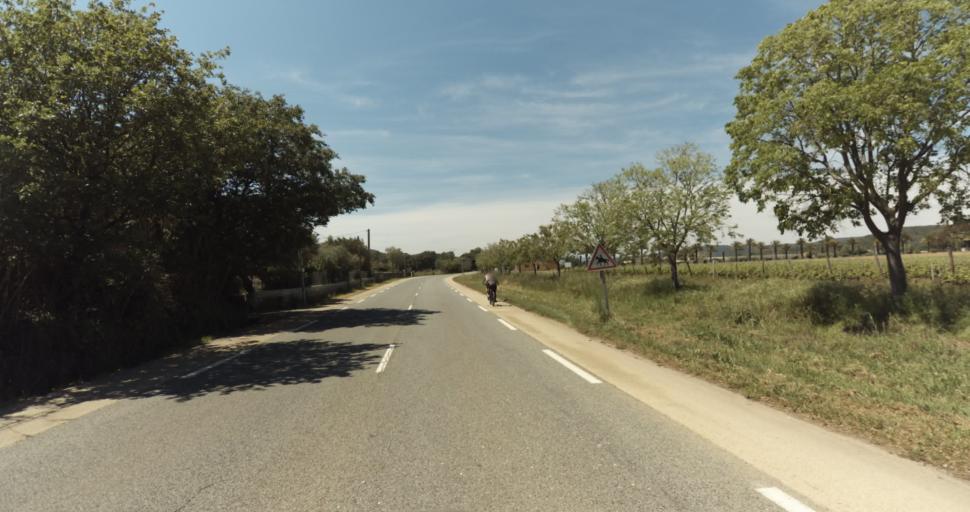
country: FR
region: Provence-Alpes-Cote d'Azur
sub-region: Departement du Var
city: Hyeres
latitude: 43.1295
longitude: 6.1795
